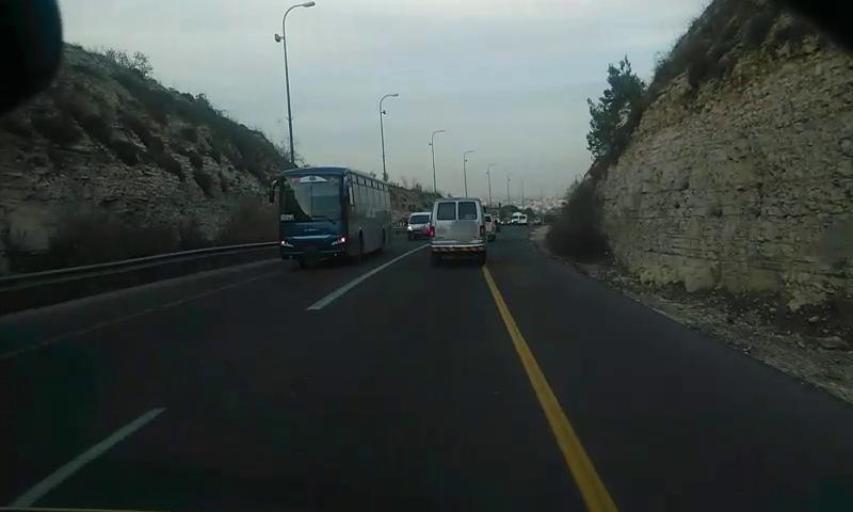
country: PS
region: West Bank
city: Al Khadir
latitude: 31.6818
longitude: 35.1541
